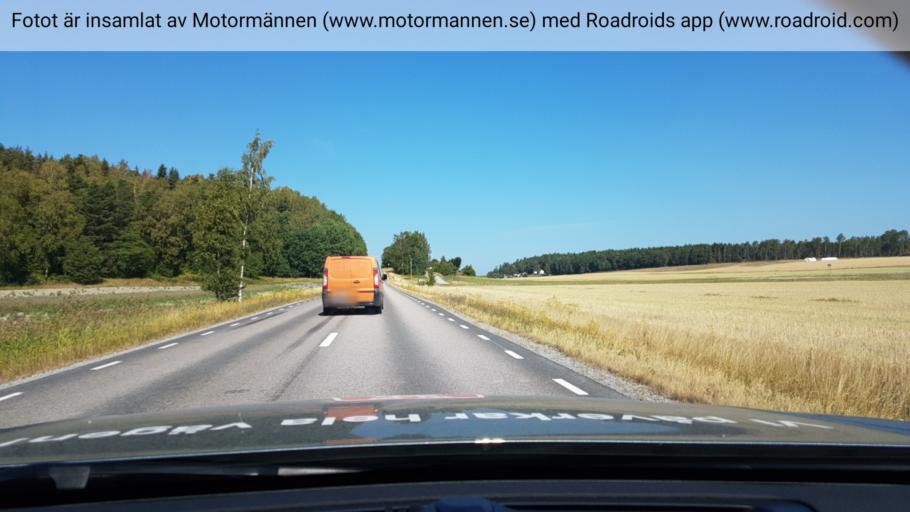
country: SE
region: Stockholm
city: Stenhamra
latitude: 59.3626
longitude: 17.6170
